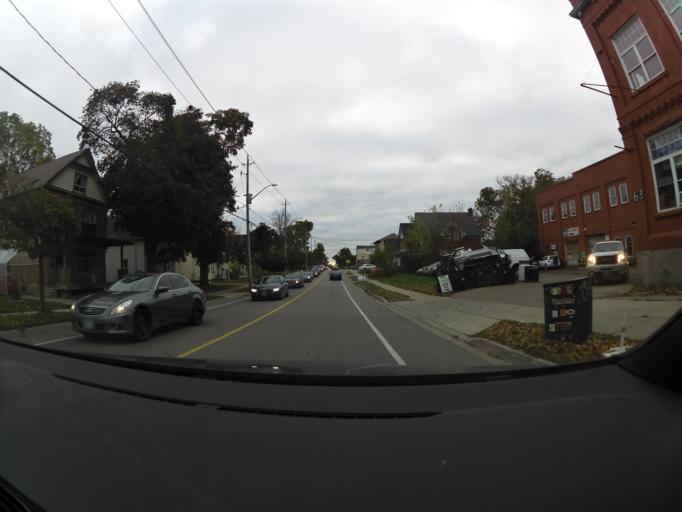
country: CA
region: Ontario
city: Kitchener
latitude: 43.4447
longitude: -80.4905
